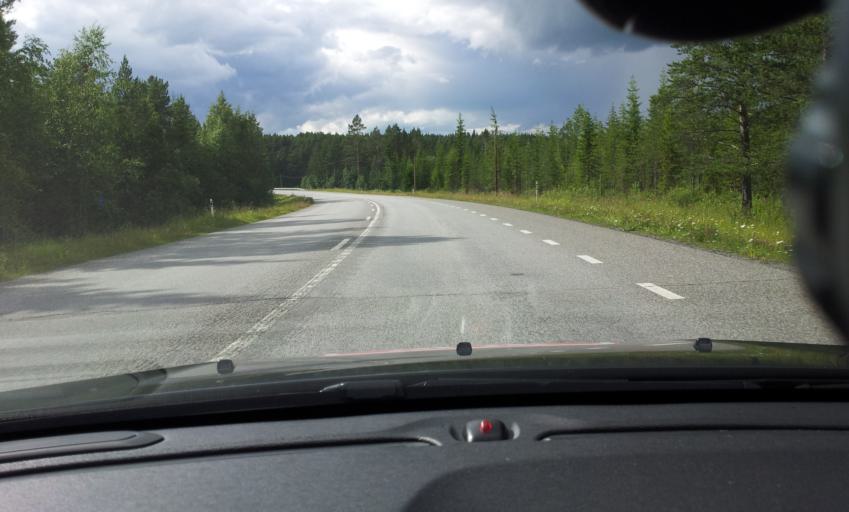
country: SE
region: Jaemtland
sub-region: Are Kommun
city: Jarpen
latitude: 63.3352
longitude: 13.5165
